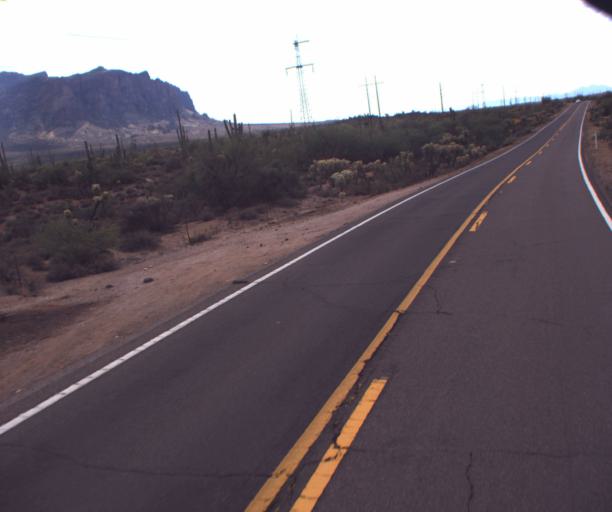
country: US
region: Arizona
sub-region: Pinal County
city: Apache Junction
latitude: 33.4855
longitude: -111.4691
